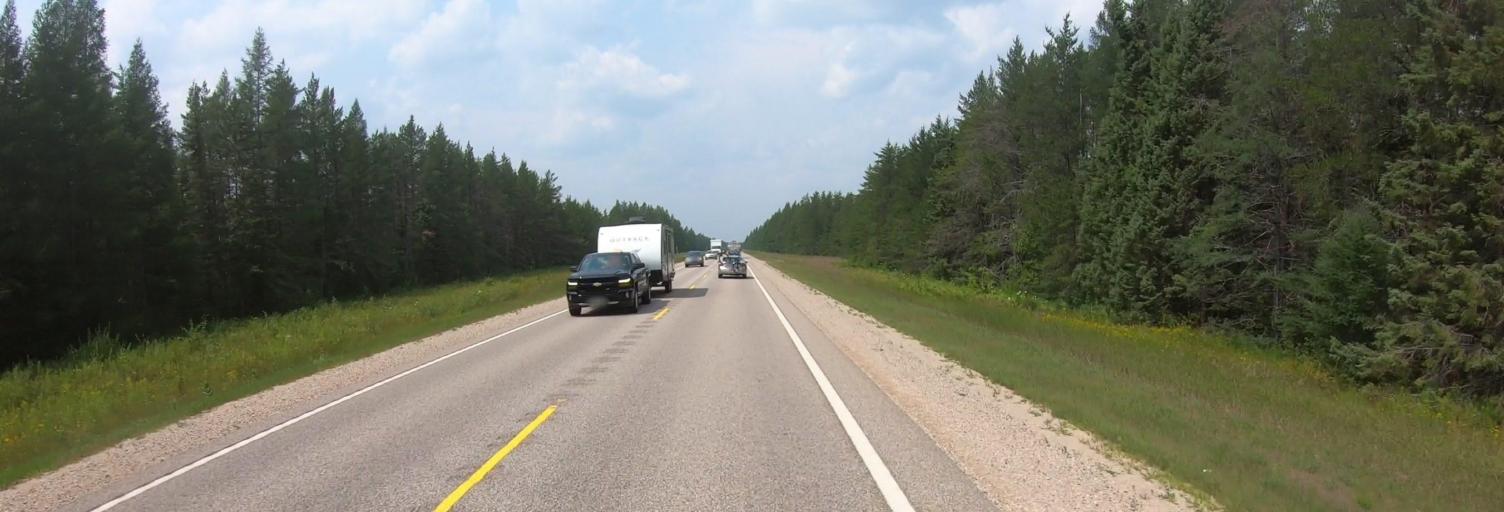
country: US
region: Michigan
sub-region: Alger County
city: Munising
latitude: 46.3464
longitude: -86.3127
